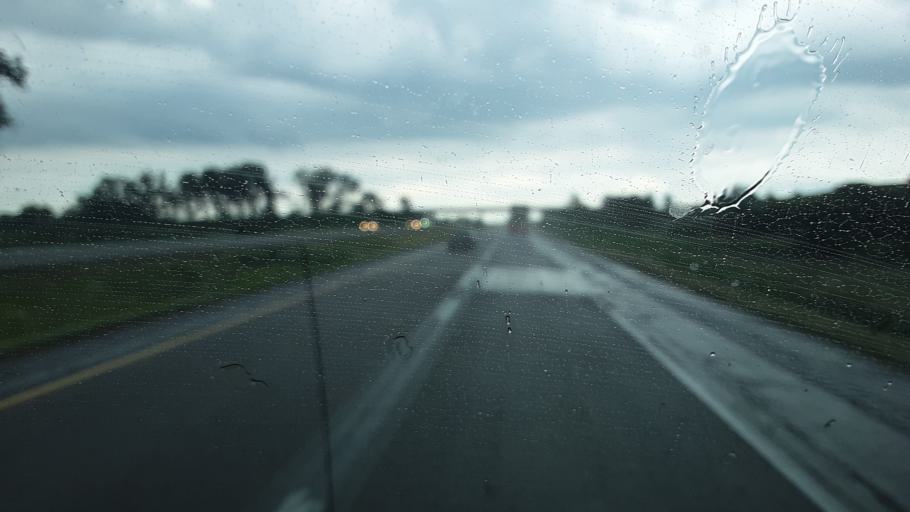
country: US
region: Iowa
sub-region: Pottawattamie County
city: Council Bluffs
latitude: 41.3146
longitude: -95.7592
